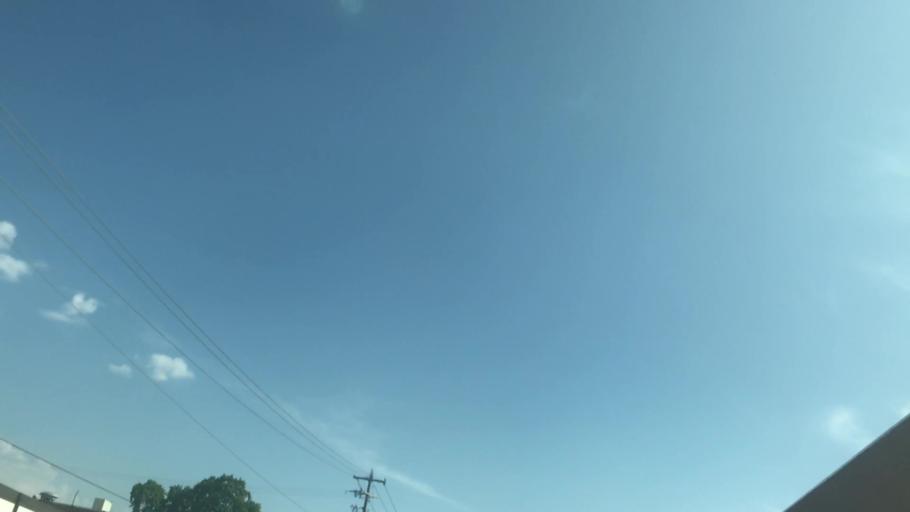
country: US
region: Wisconsin
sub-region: Brown County
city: Allouez
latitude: 44.4919
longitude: -88.0381
